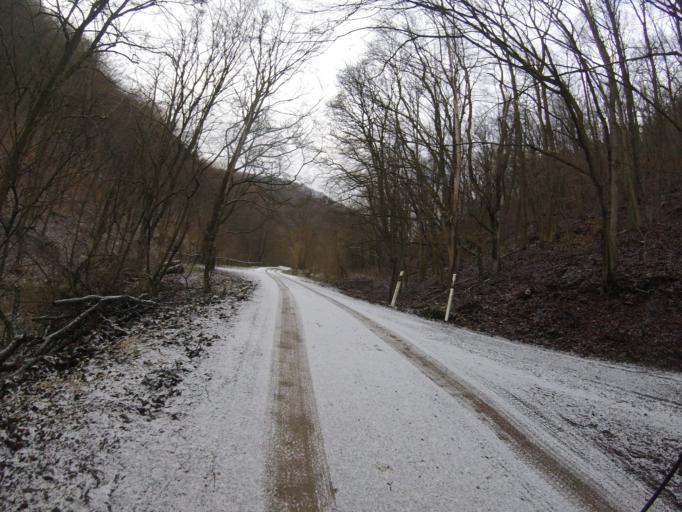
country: HU
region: Pest
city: Visegrad
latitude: 47.7576
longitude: 18.9836
